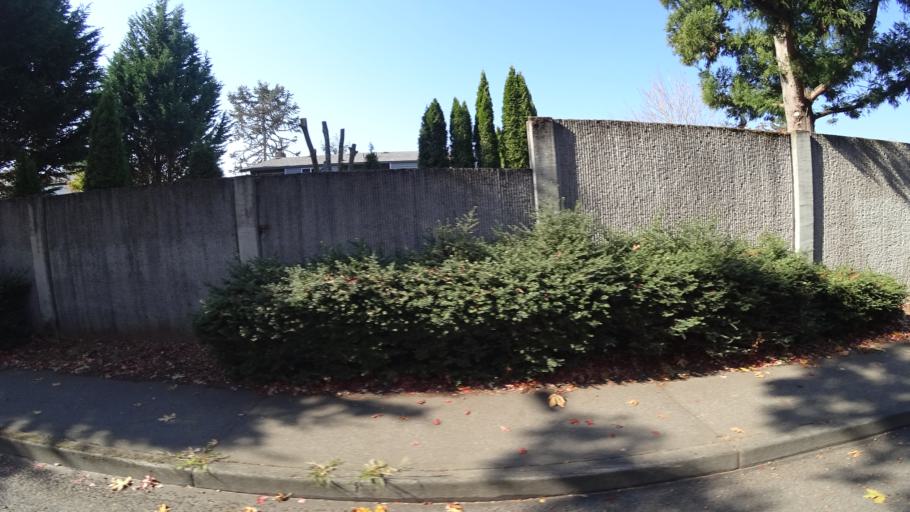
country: US
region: Oregon
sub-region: Multnomah County
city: Gresham
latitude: 45.4908
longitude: -122.4479
